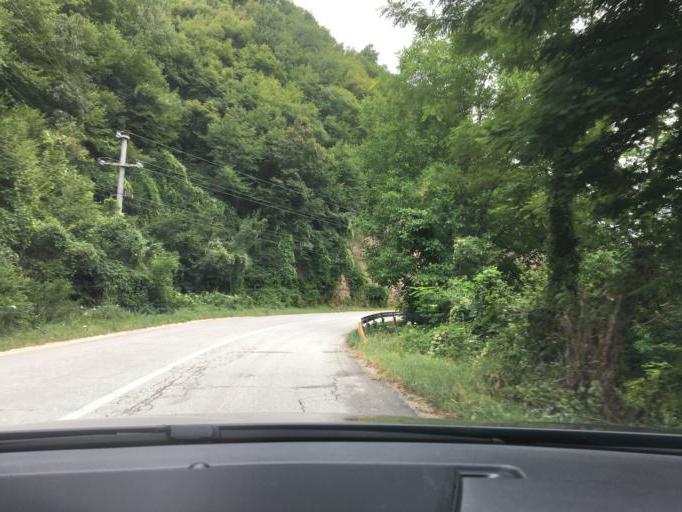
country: MK
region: Kriva Palanka
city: Kriva Palanka
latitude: 42.2169
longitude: 22.3514
